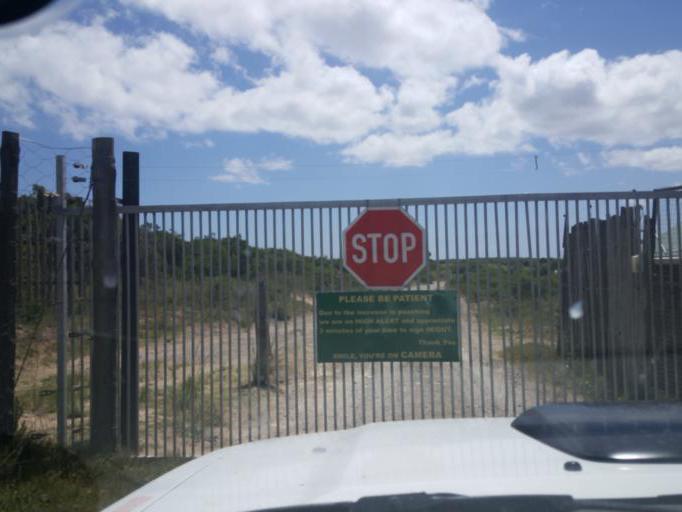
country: ZA
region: Eastern Cape
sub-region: Cacadu District Municipality
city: Grahamstown
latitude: -33.5721
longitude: 26.1342
